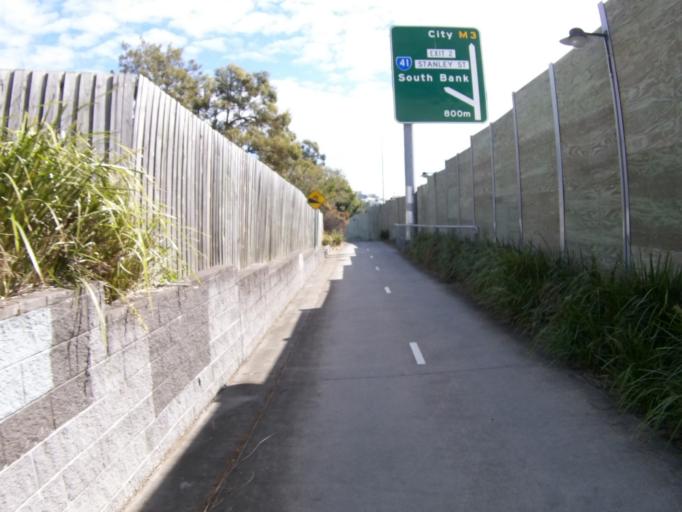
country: AU
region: Queensland
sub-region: Brisbane
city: Woolloongabba
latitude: -27.4946
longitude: 153.0366
